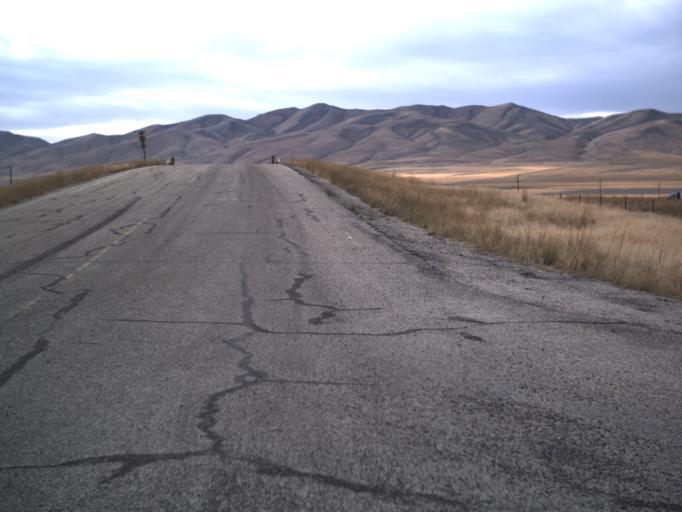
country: US
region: Utah
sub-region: Box Elder County
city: Garland
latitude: 41.8420
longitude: -112.4357
